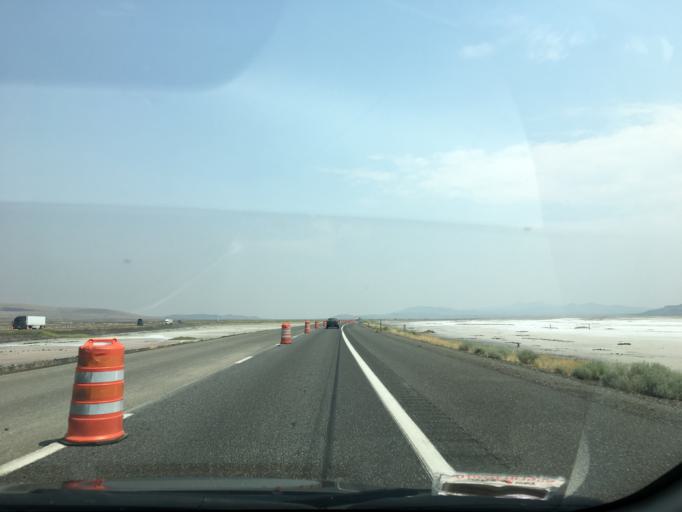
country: US
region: Nevada
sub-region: Lyon County
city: Fernley
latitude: 39.7050
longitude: -119.0970
